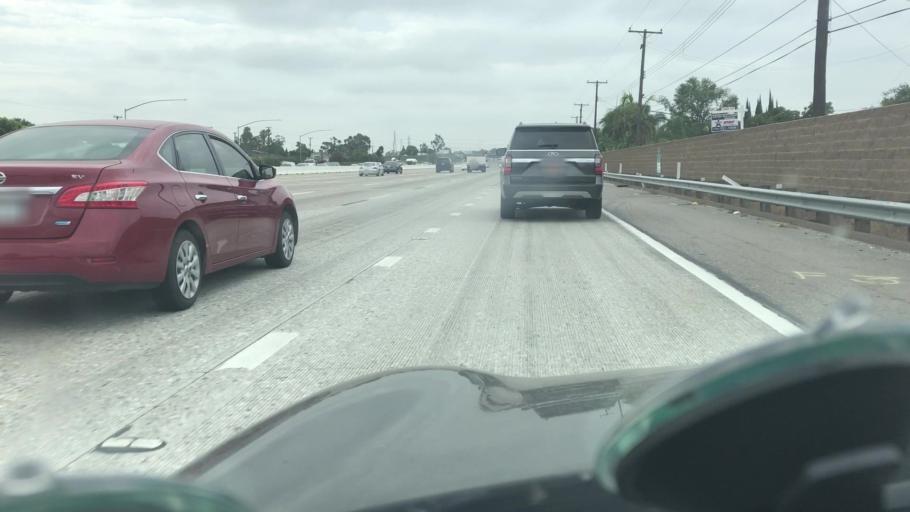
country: US
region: California
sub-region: Orange County
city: Anaheim
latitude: 33.8237
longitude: -117.8764
